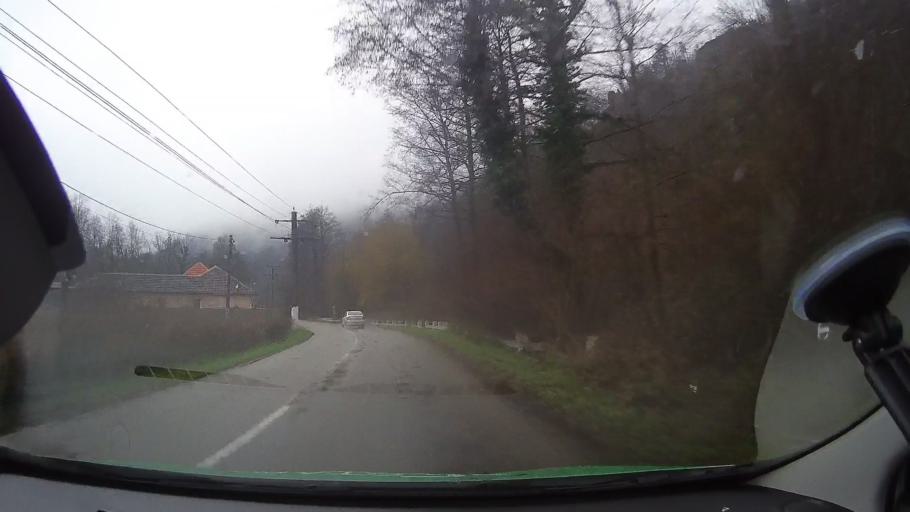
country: RO
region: Arad
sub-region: Comuna Dezna
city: Dezna
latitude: 46.4144
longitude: 22.2549
